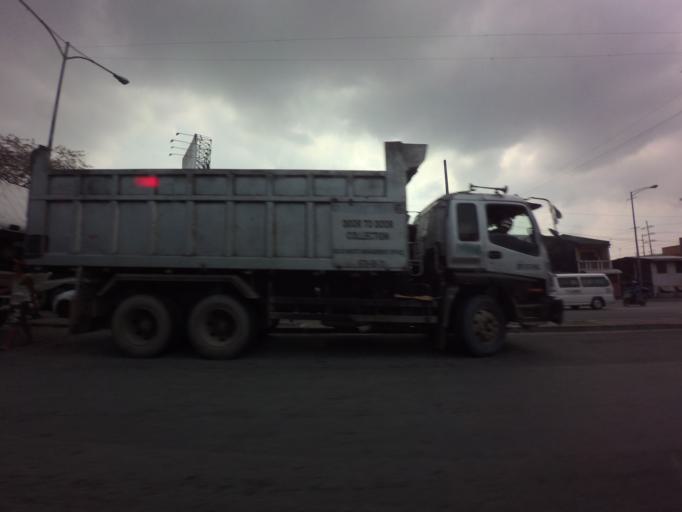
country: PH
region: Calabarzon
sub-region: Province of Rizal
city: Pateros
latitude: 14.5558
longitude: 121.0634
